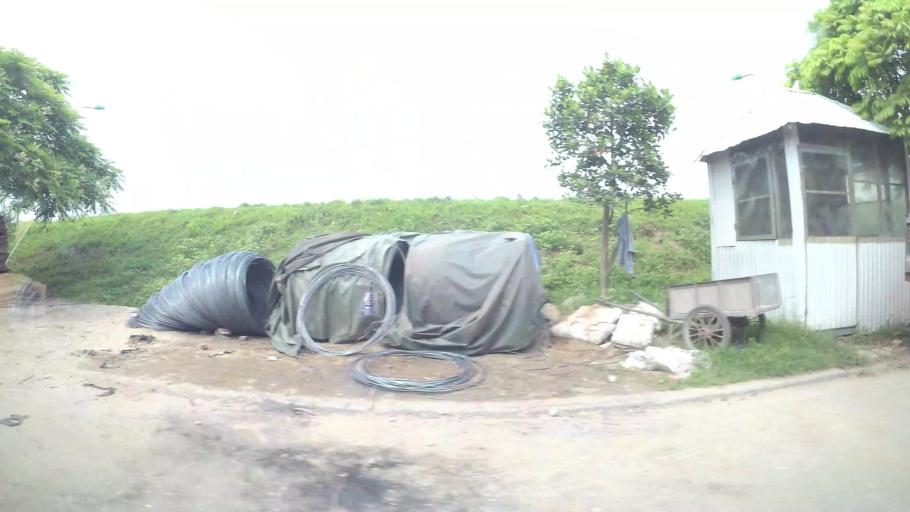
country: VN
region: Ha Noi
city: Trau Quy
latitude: 21.0726
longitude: 105.9161
